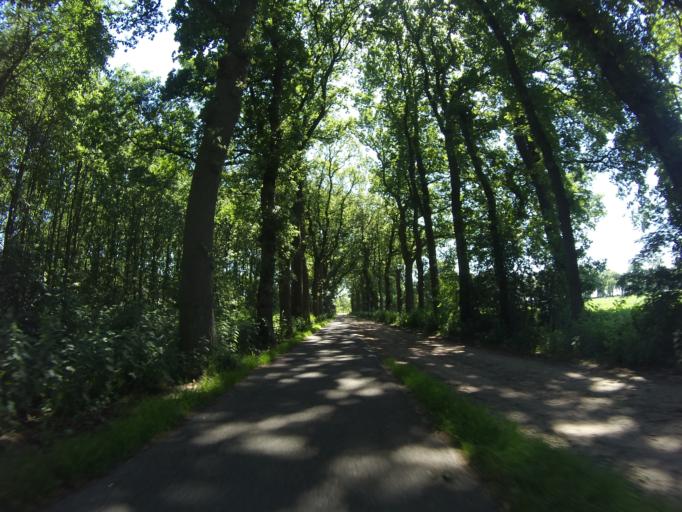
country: NL
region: Drenthe
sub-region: Gemeente Coevorden
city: Sleen
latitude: 52.7615
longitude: 6.8333
